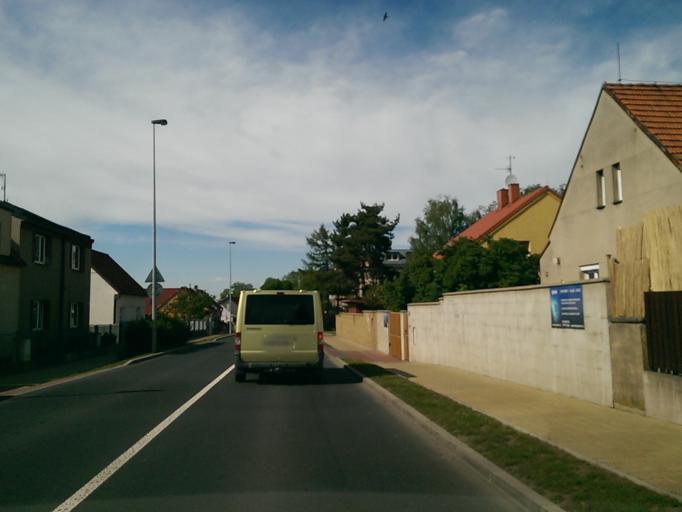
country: CZ
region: Praha
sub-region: Praha 20
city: Horni Pocernice
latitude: 50.1140
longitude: 14.6260
